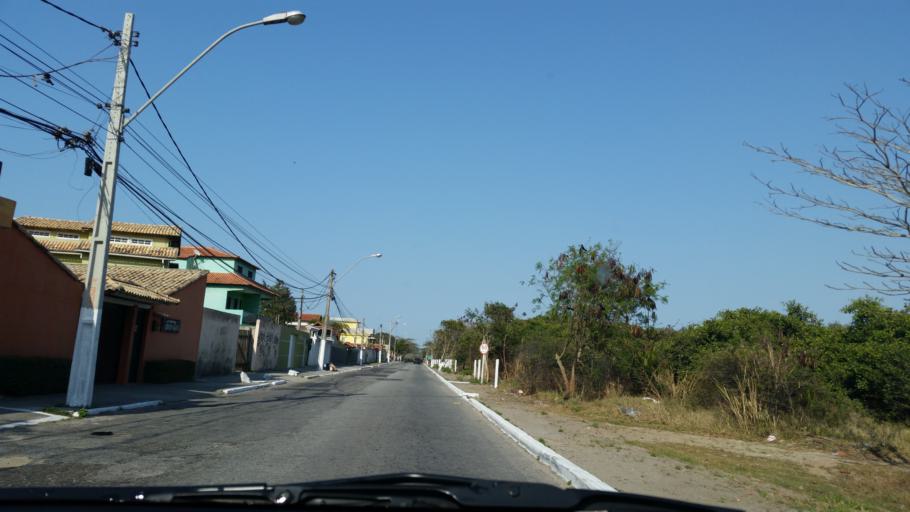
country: BR
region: Rio de Janeiro
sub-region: Cabo Frio
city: Cabo Frio
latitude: -22.8638
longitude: -41.9986
